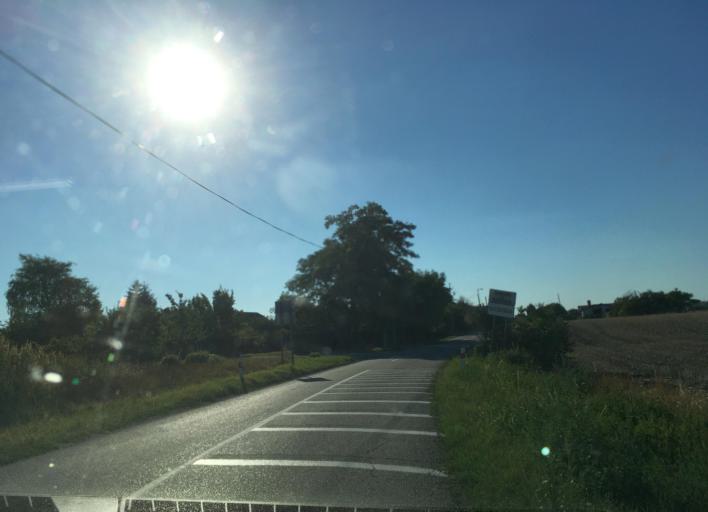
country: SK
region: Trnavsky
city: Samorin
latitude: 48.0297
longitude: 17.3392
